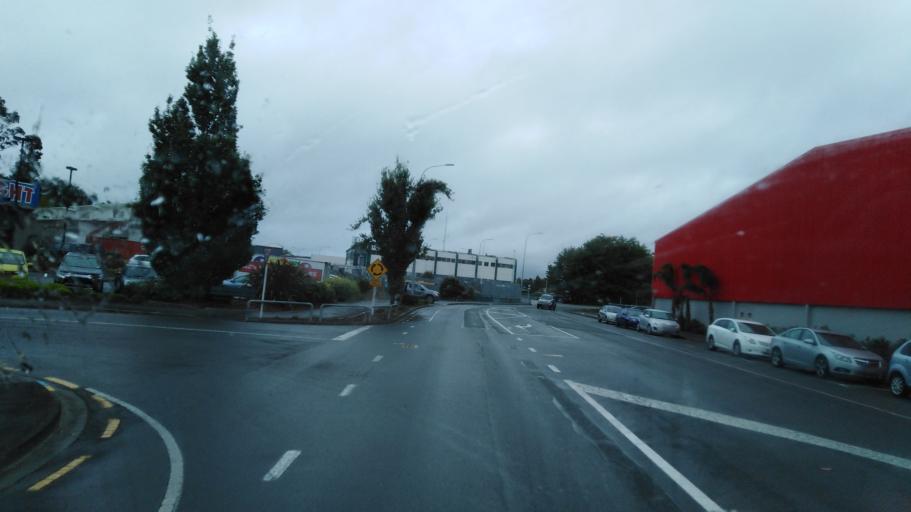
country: NZ
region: Nelson
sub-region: Nelson City
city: Nelson
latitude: -41.2718
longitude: 173.2779
